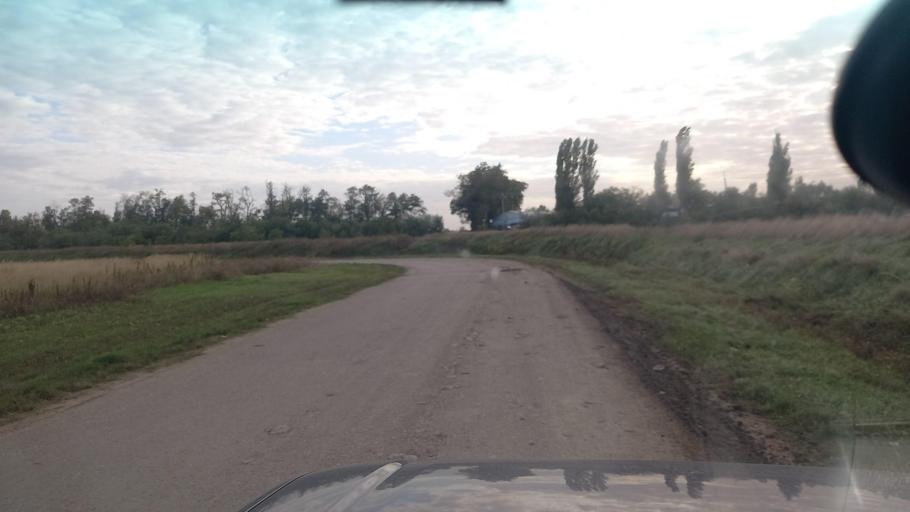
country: RU
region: Krasnodarskiy
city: Krasnodar
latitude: 45.1282
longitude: 38.9097
